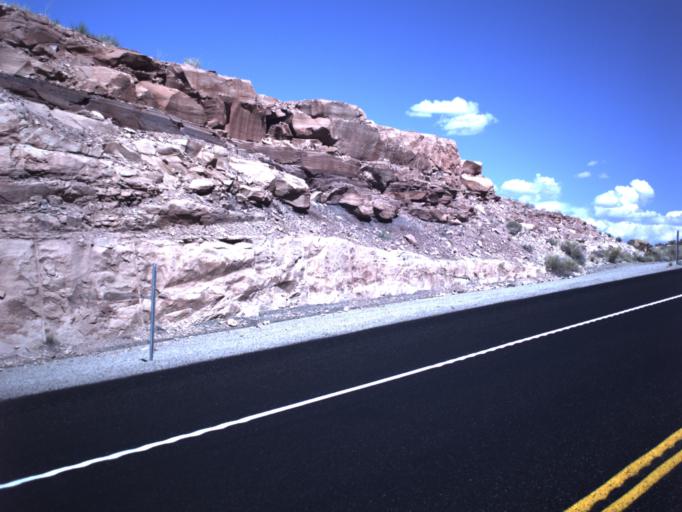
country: US
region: Utah
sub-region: Grand County
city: Moab
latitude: 38.6476
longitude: -109.7375
